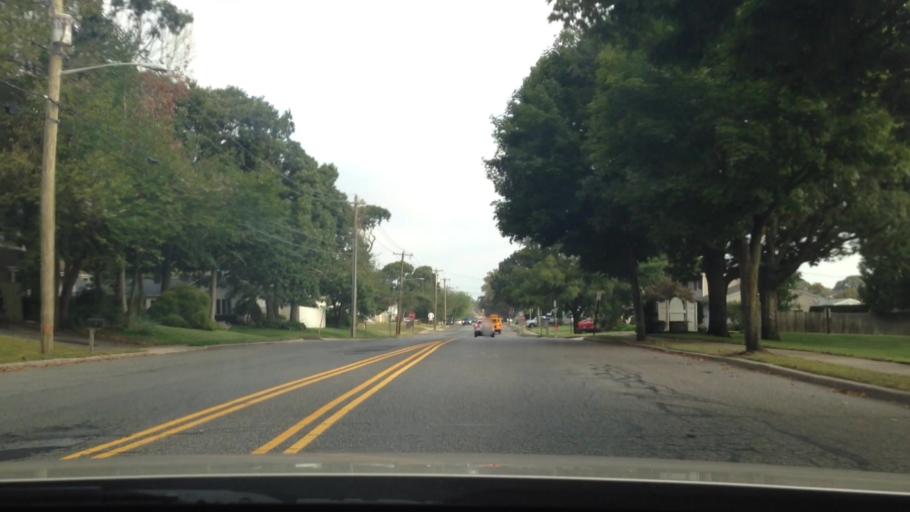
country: US
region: New York
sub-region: Suffolk County
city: Selden
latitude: 40.8563
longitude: -73.0464
